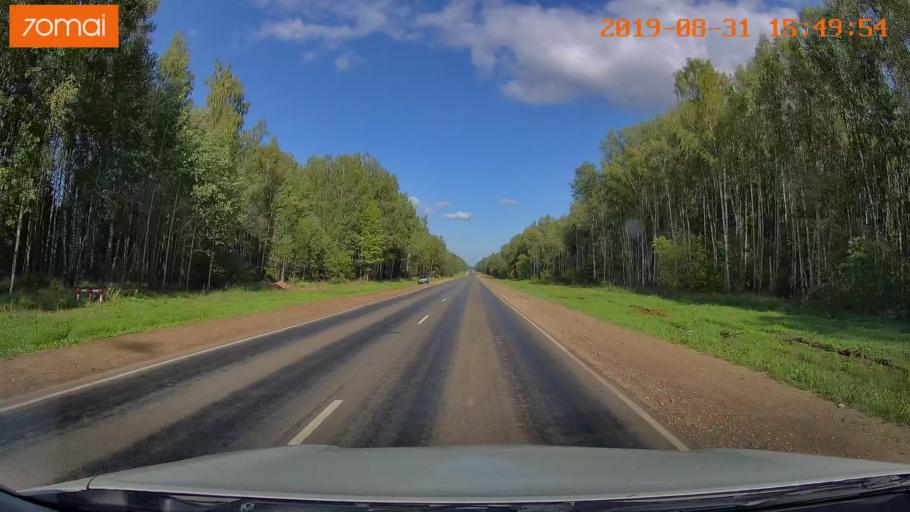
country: RU
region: Kaluga
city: Yukhnov
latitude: 54.6937
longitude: 35.0603
